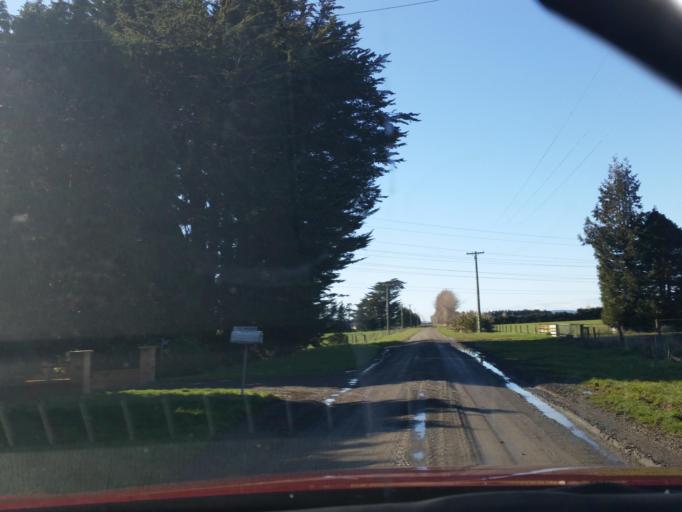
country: NZ
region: Southland
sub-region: Southland District
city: Winton
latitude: -46.1700
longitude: 168.1575
